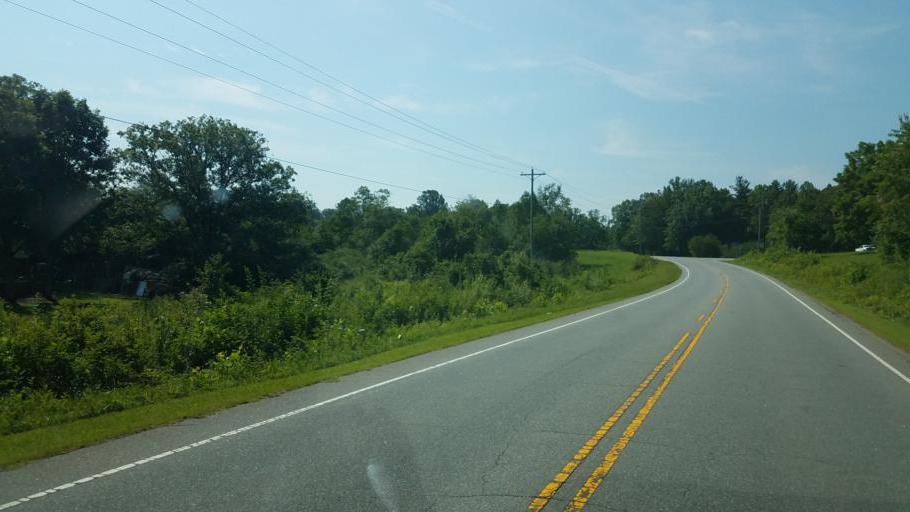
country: US
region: North Carolina
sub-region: Burke County
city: Glen Alpine
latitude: 35.8067
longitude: -81.7876
